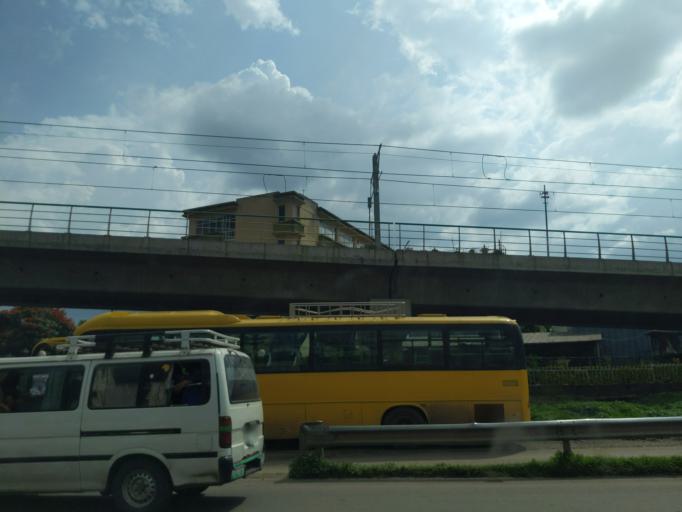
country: ET
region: Adis Abeba
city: Addis Ababa
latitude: 8.9775
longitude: 38.7596
